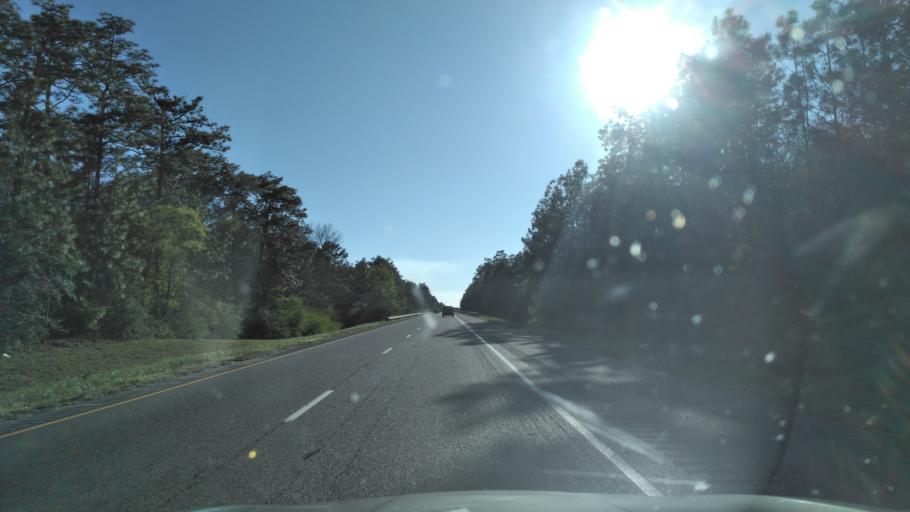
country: US
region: Alabama
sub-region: Escambia County
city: Atmore
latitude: 31.0556
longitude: -87.5864
